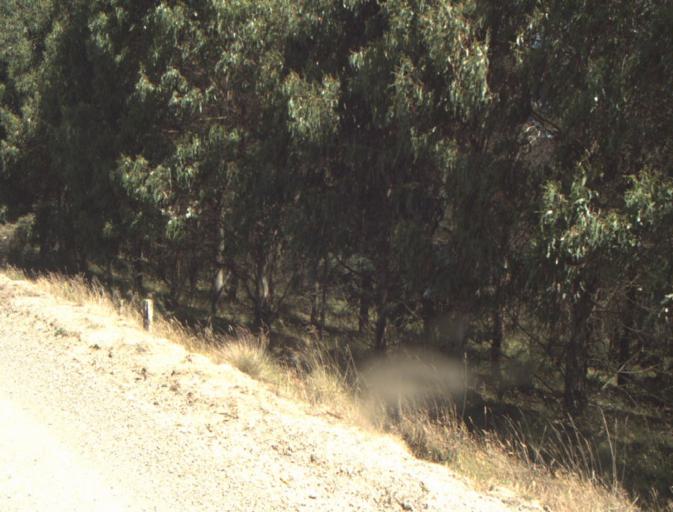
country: AU
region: Tasmania
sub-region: Dorset
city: Scottsdale
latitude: -41.3555
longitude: 147.4559
